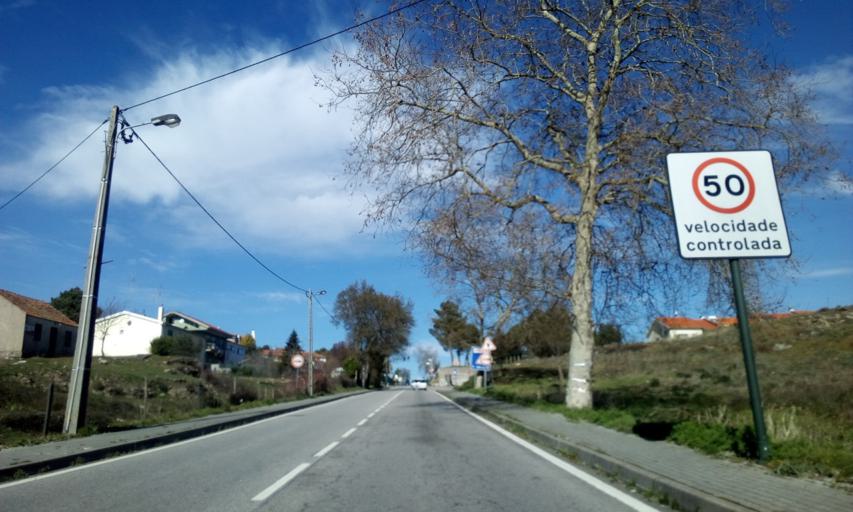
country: PT
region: Guarda
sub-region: Guarda
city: Sequeira
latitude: 40.5639
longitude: -7.2271
